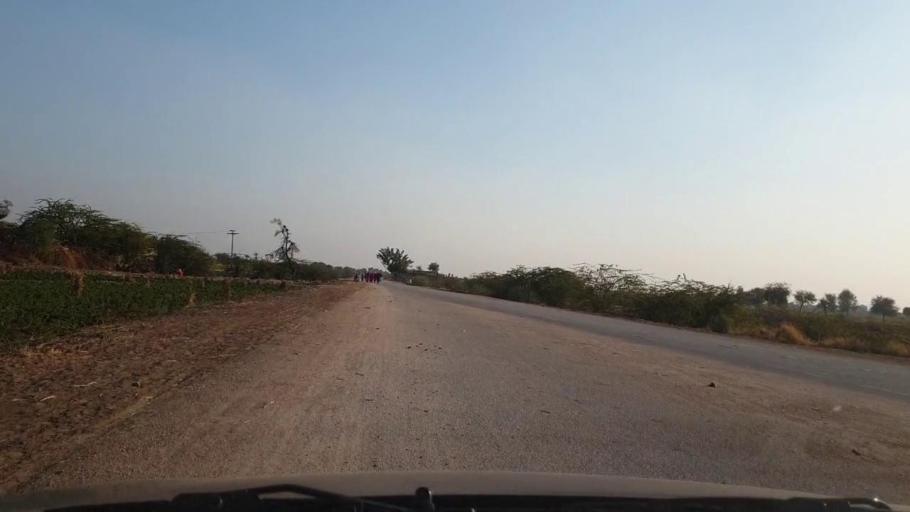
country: PK
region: Sindh
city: Jhol
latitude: 25.9208
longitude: 68.9084
